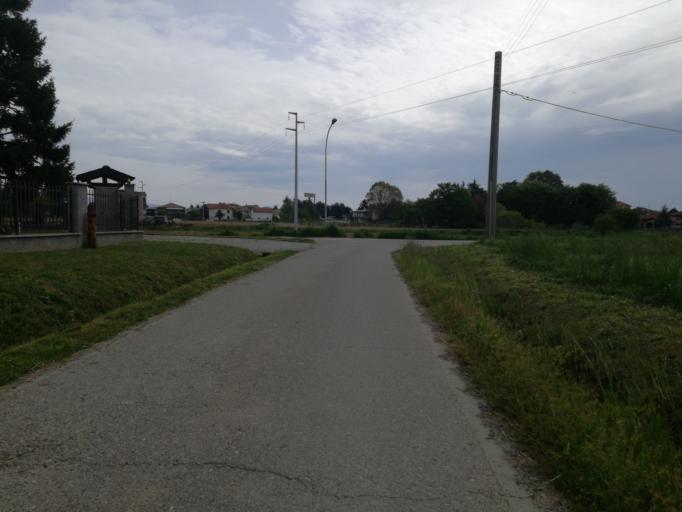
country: IT
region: Lombardy
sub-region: Provincia di Monza e Brianza
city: Porto d'Adda
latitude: 45.6510
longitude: 9.4576
